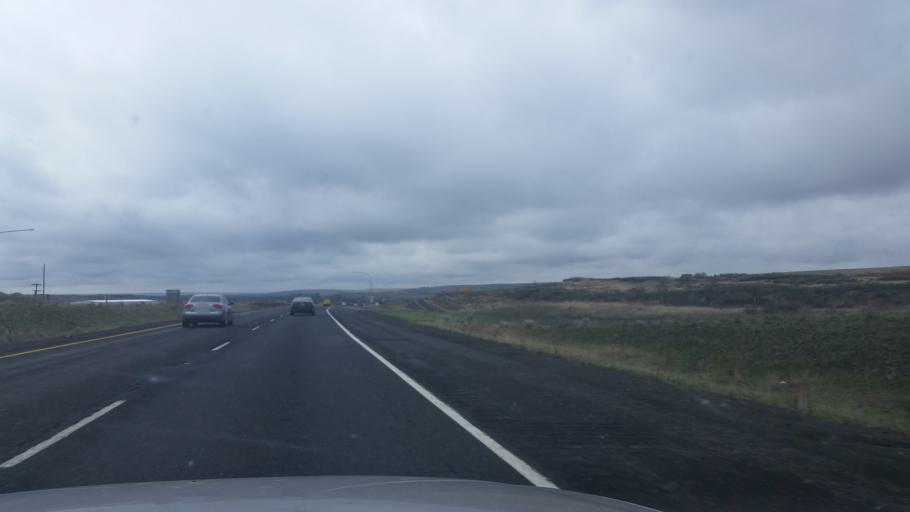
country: US
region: Washington
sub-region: Lincoln County
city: Davenport
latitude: 47.3074
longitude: -117.9750
